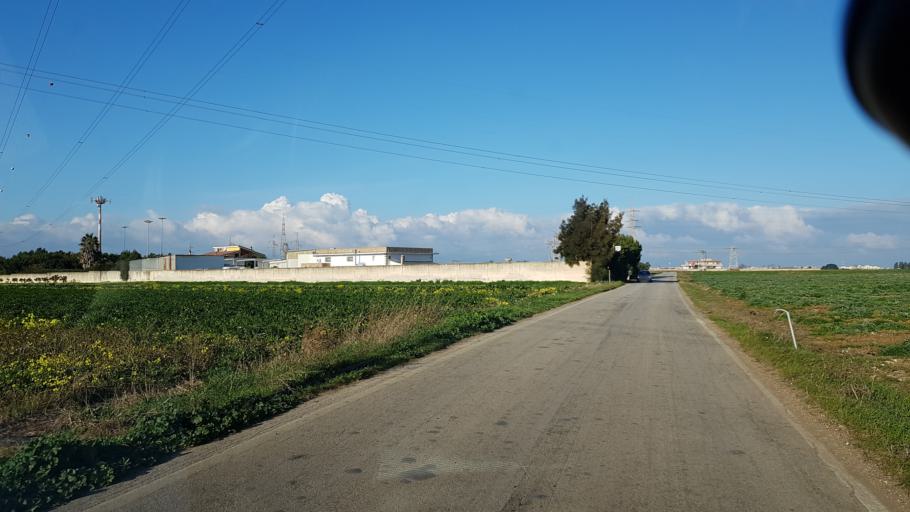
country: IT
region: Apulia
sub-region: Provincia di Brindisi
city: Brindisi
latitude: 40.5972
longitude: 17.9053
